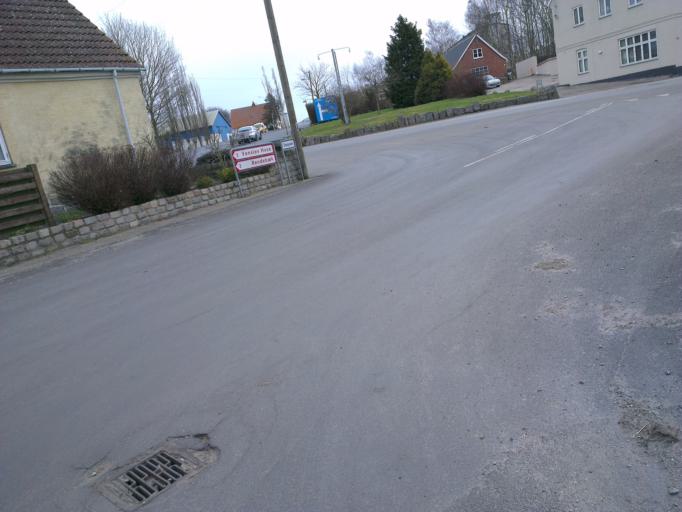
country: DK
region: Capital Region
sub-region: Frederikssund Kommune
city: Skibby
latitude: 55.7760
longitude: 11.9055
